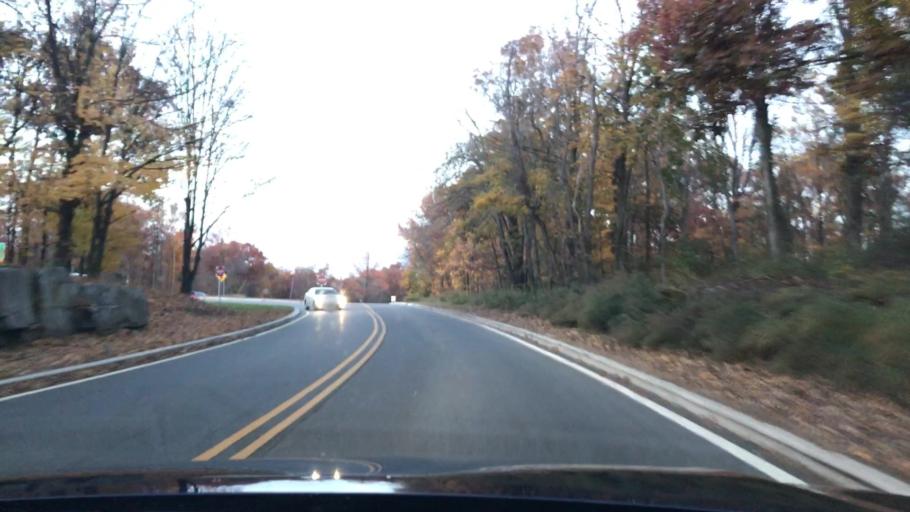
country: US
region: New Jersey
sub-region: Bergen County
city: Alpine
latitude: 40.9557
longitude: -73.9193
